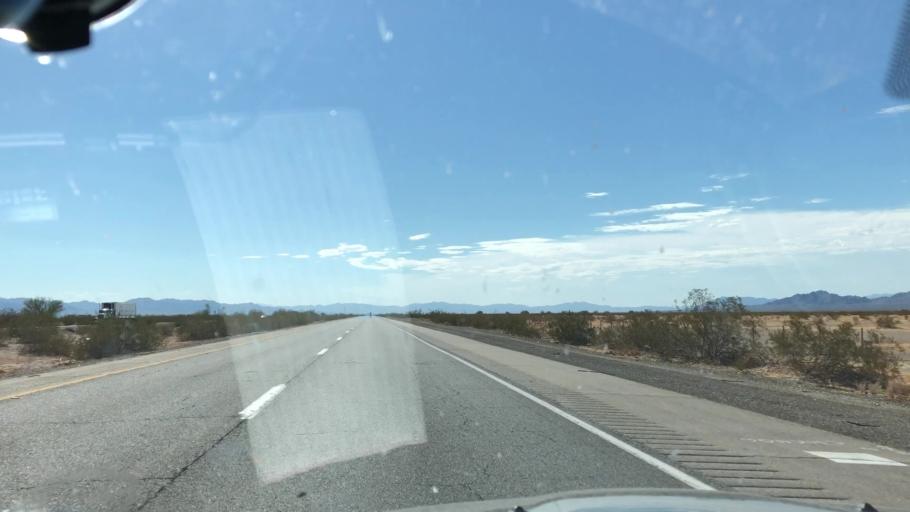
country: US
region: California
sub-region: Riverside County
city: Mesa Verde
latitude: 33.6123
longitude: -115.0060
